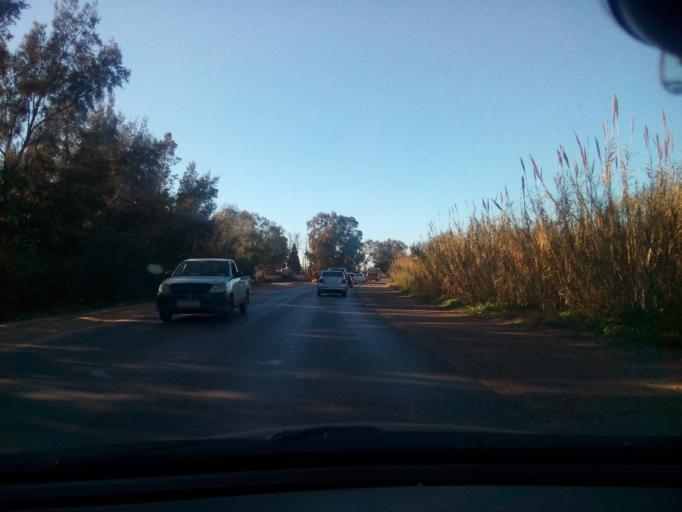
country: DZ
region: Mostaganem
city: Mostaganem
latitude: 35.9013
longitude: 0.2151
